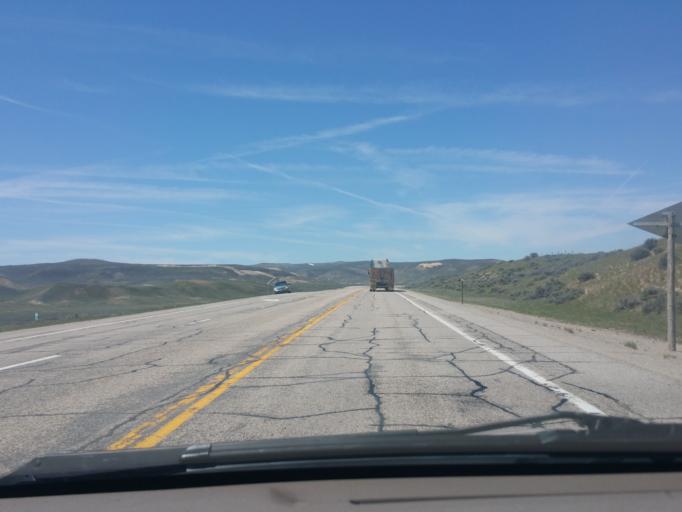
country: US
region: Wyoming
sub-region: Lincoln County
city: Kemmerer
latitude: 41.8139
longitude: -110.6694
